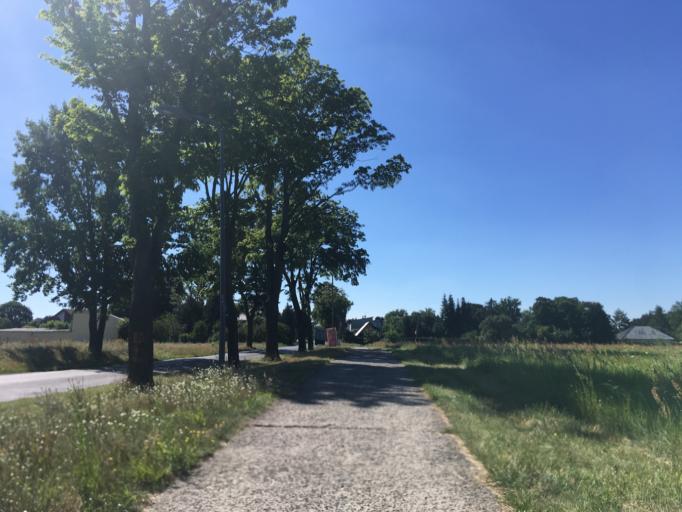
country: DE
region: Brandenburg
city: Petershagen
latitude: 52.5173
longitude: 13.7701
